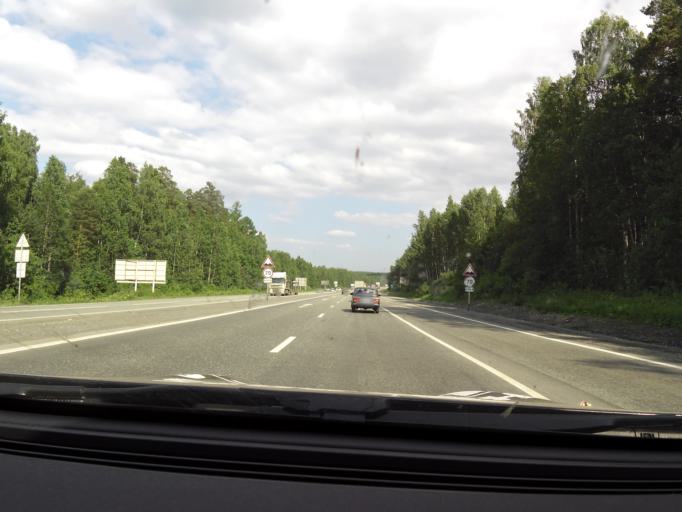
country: RU
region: Sverdlovsk
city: Talitsa
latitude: 56.8488
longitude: 60.0661
